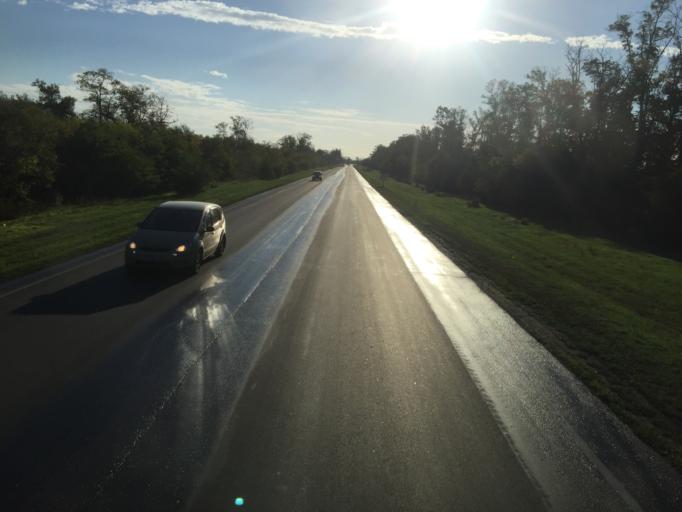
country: RU
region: Rostov
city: Mechetinskaya
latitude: 46.7599
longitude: 40.4412
